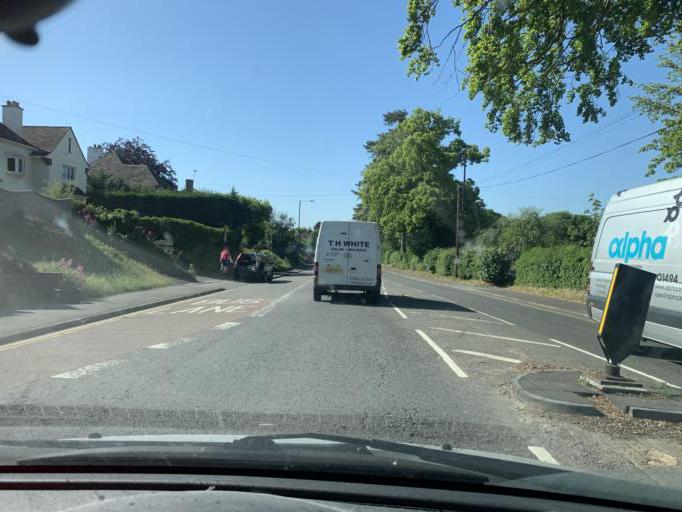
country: GB
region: England
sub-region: Wiltshire
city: Salisbury
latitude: 51.0826
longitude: -1.7972
